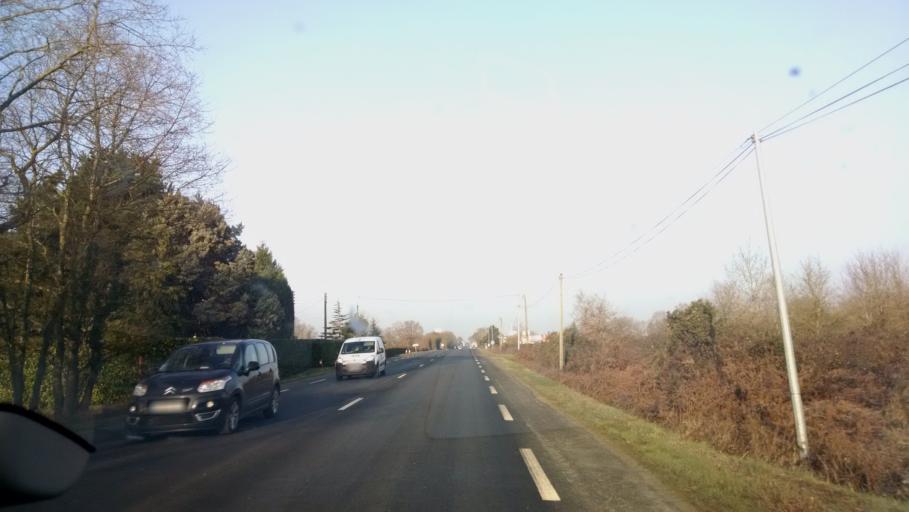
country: FR
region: Pays de la Loire
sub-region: Departement de la Loire-Atlantique
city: Aigrefeuille-sur-Maine
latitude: 47.0862
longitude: -1.4239
